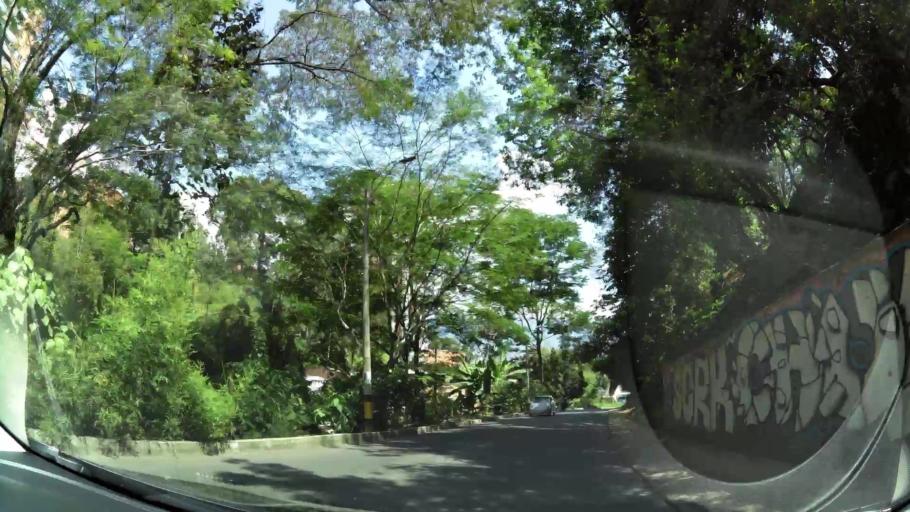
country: CO
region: Antioquia
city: Itagui
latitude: 6.2163
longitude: -75.6033
